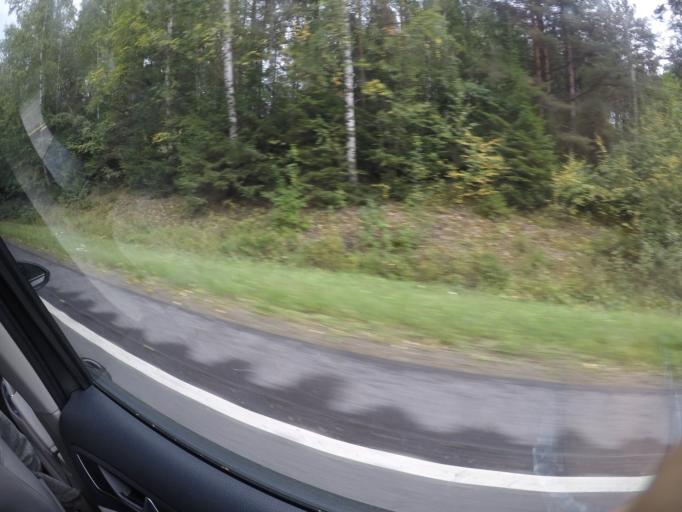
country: FI
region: Haeme
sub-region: Haemeenlinna
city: Parola
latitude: 61.0766
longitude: 24.3923
